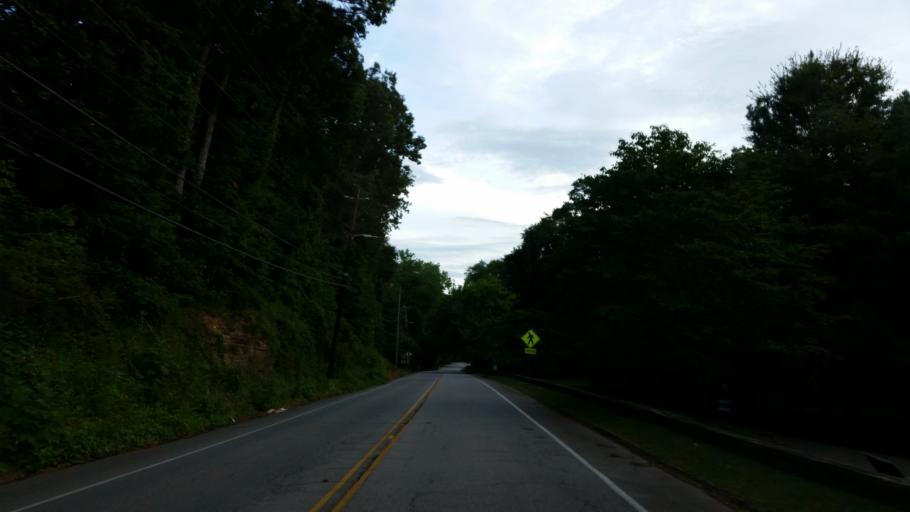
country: US
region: Georgia
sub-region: DeKalb County
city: North Atlanta
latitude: 33.8695
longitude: -84.3875
